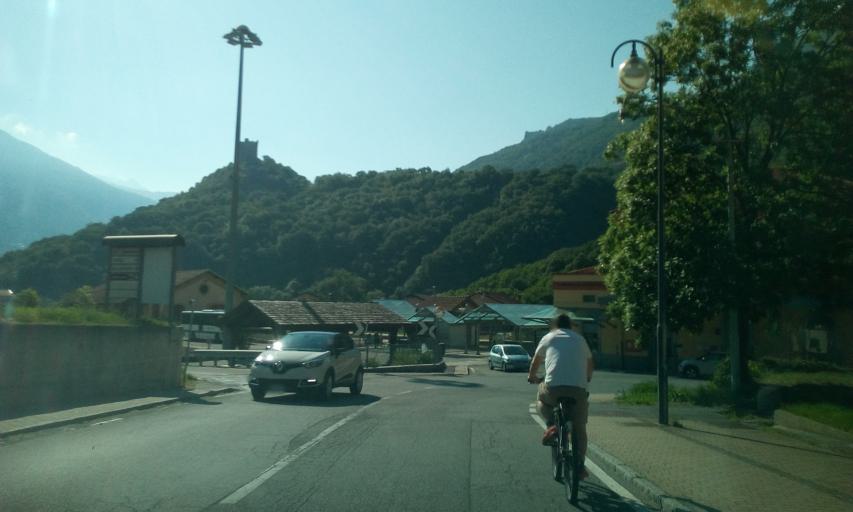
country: IT
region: Aosta Valley
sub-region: Valle d'Aosta
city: Chatillon
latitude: 45.7439
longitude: 7.6189
